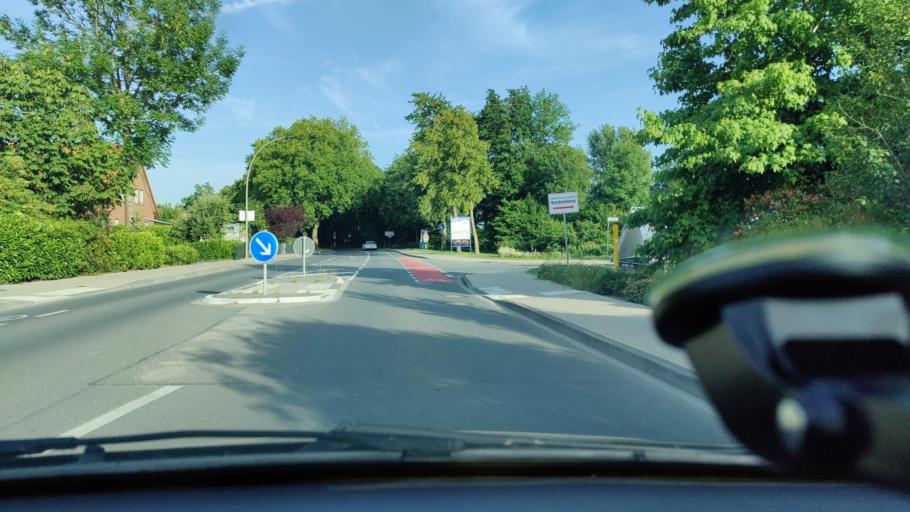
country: DE
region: North Rhine-Westphalia
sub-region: Regierungsbezirk Munster
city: Billerbeck
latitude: 51.9801
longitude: 7.2785
